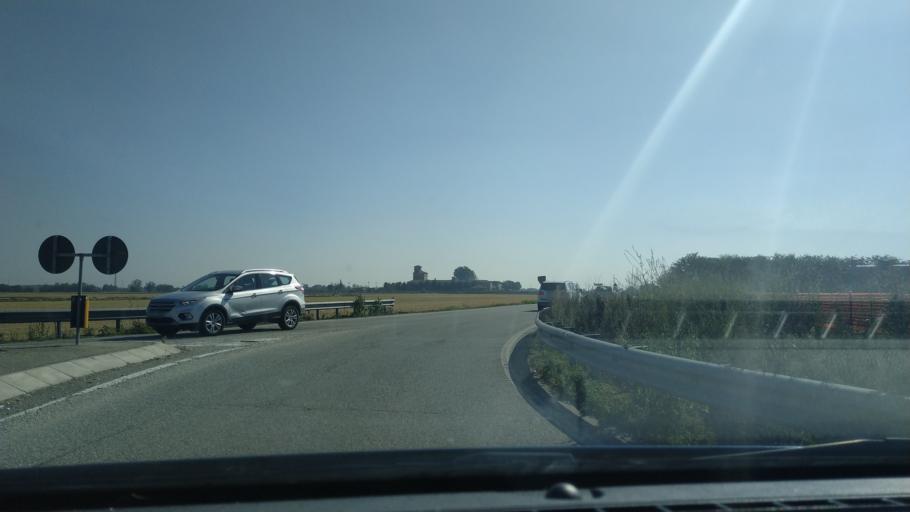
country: IT
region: Piedmont
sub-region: Provincia di Alessandria
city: Borgo San Martino
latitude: 45.1008
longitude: 8.5270
